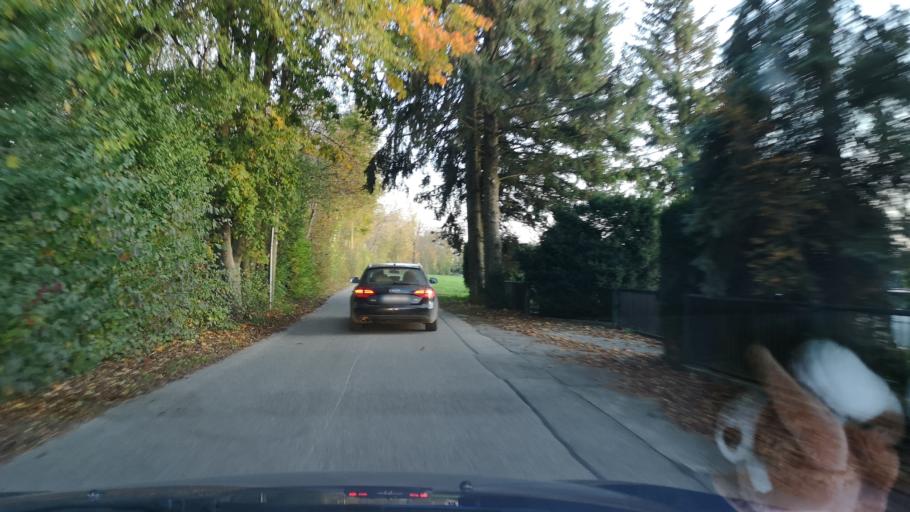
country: DE
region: Bavaria
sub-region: Upper Bavaria
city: Eichenried
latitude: 48.2345
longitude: 11.7547
